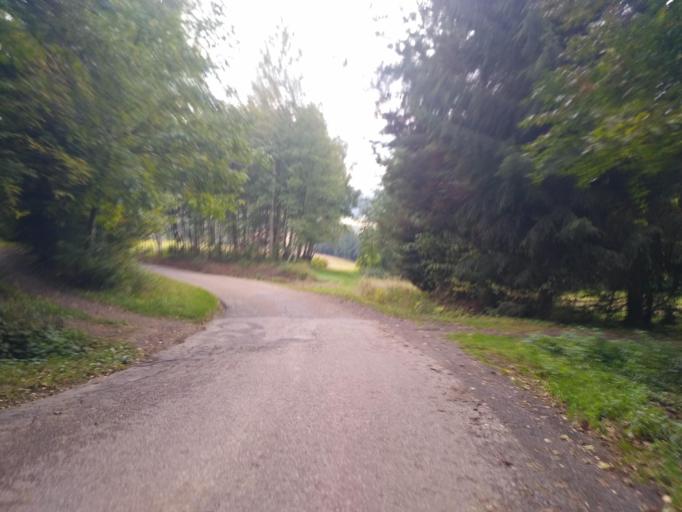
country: PL
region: Subcarpathian Voivodeship
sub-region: Powiat ropczycko-sedziszowski
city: Niedzwiada
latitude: 49.9417
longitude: 21.4622
